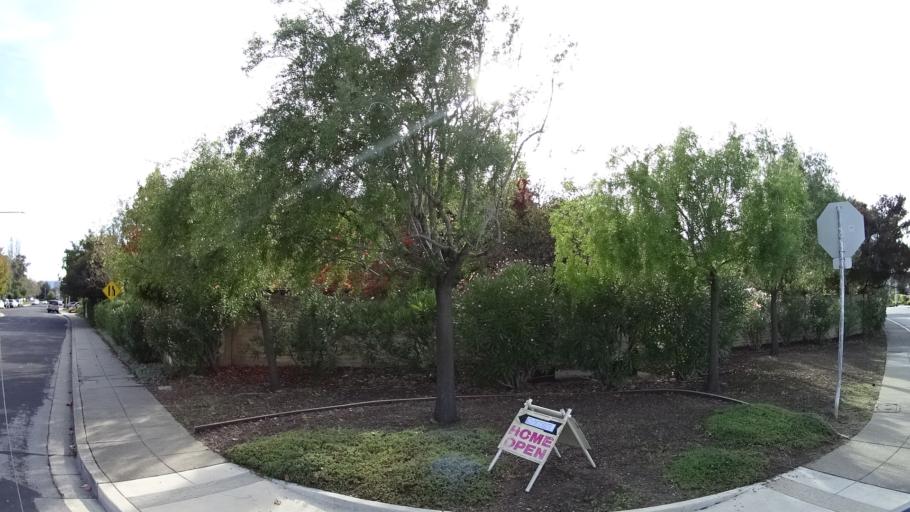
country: US
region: California
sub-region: San Mateo County
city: Foster City
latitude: 37.5486
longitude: -122.2642
